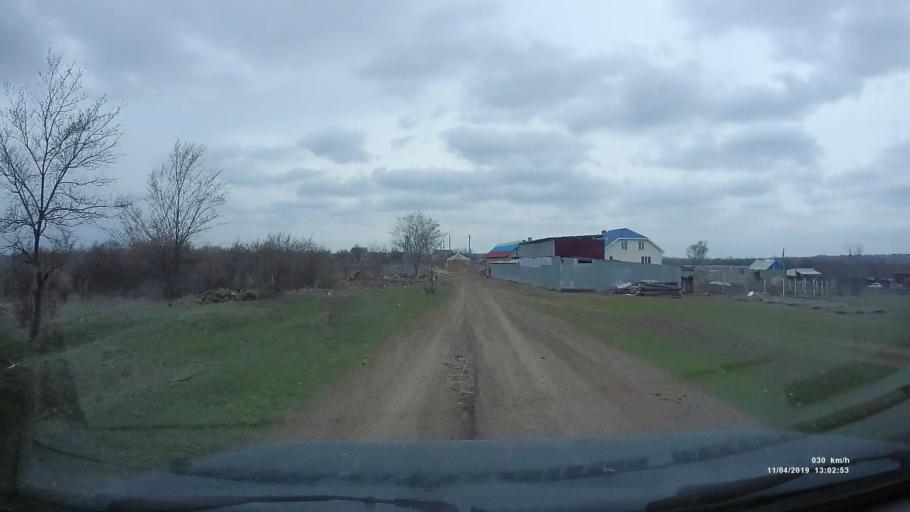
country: RU
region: Rostov
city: Staraya Stanitsa
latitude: 48.2880
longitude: 40.3544
